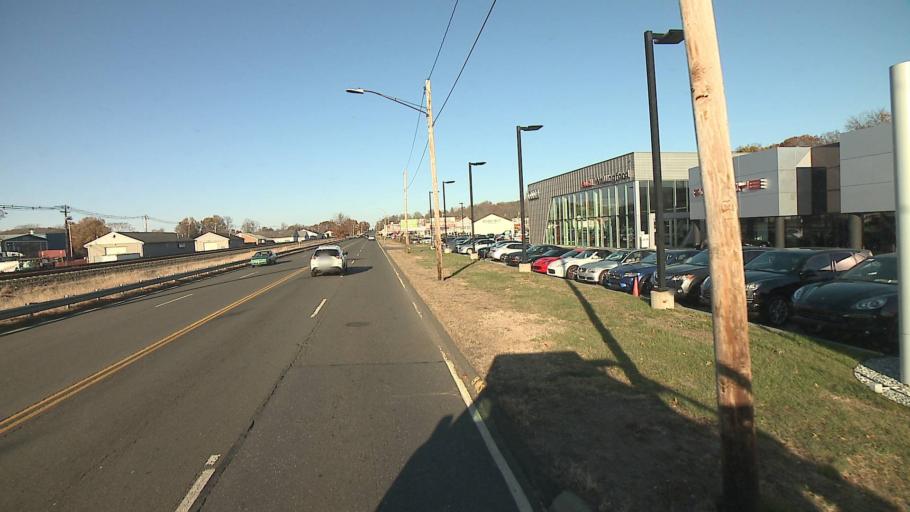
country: US
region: Connecticut
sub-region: New Haven County
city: Wallingford Center
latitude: 41.4395
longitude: -72.8324
